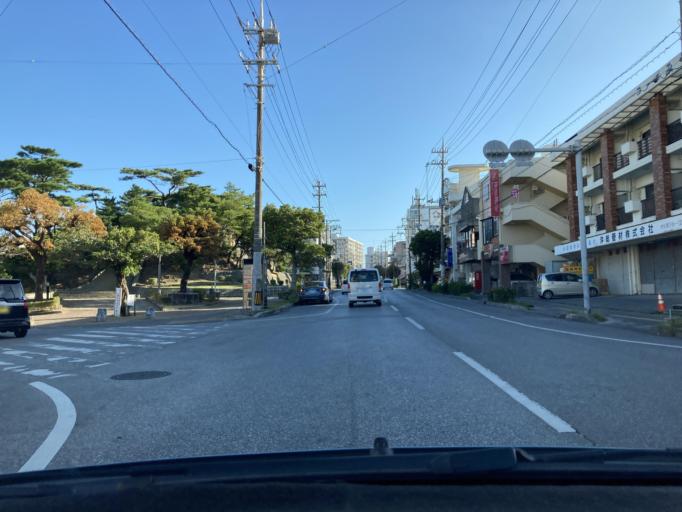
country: JP
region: Okinawa
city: Ginowan
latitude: 26.2568
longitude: 127.7133
